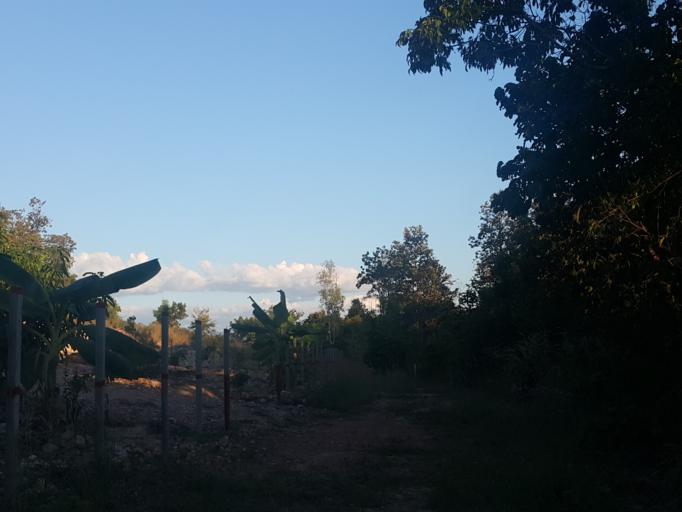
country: TH
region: Chiang Mai
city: San Sai
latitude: 18.8654
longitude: 99.1460
